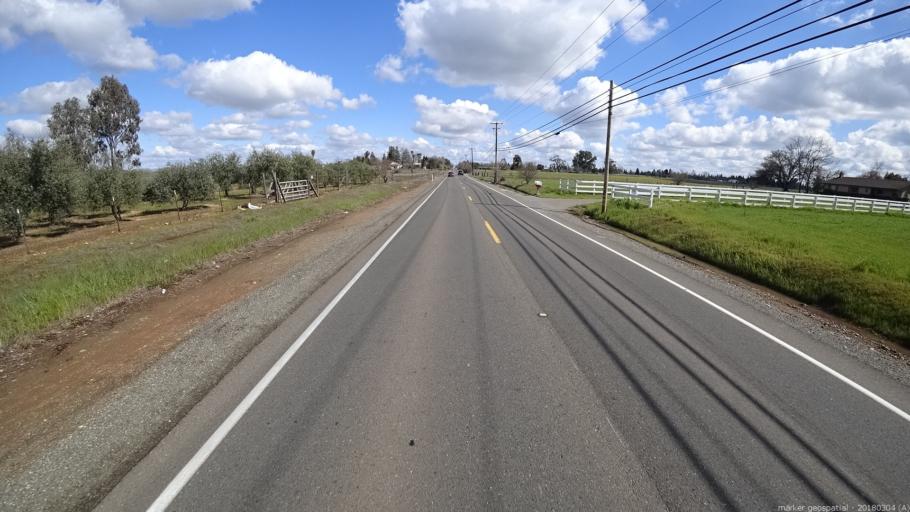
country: US
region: California
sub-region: Sacramento County
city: Vineyard
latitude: 38.4817
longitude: -121.3226
